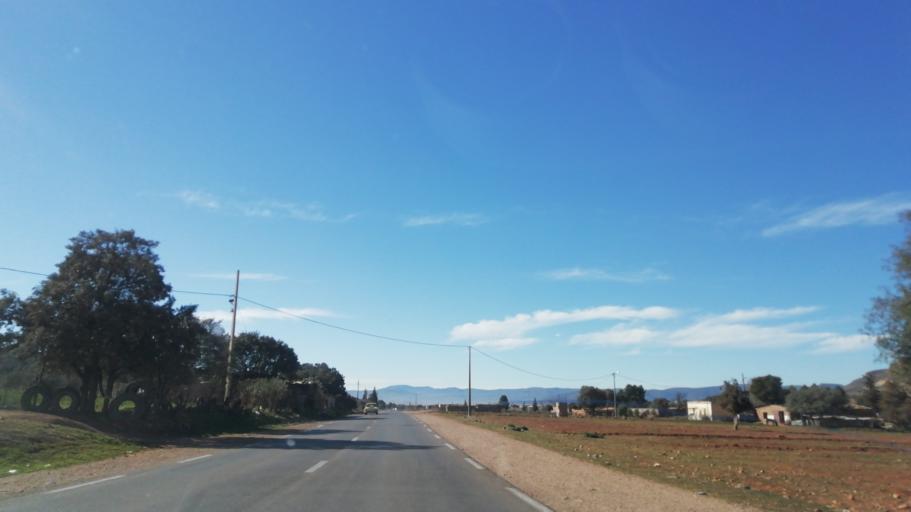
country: DZ
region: Tlemcen
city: Sebdou
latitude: 34.6925
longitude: -1.2399
